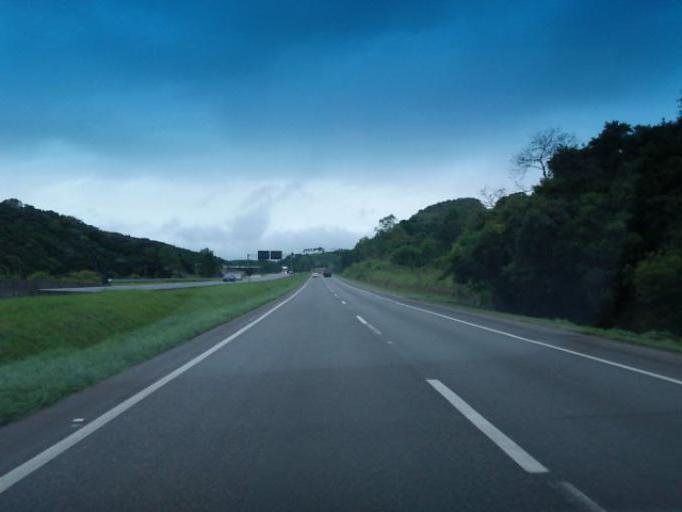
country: BR
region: Parana
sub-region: Campina Grande Do Sul
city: Campina Grande do Sul
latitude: -25.1255
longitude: -48.8568
